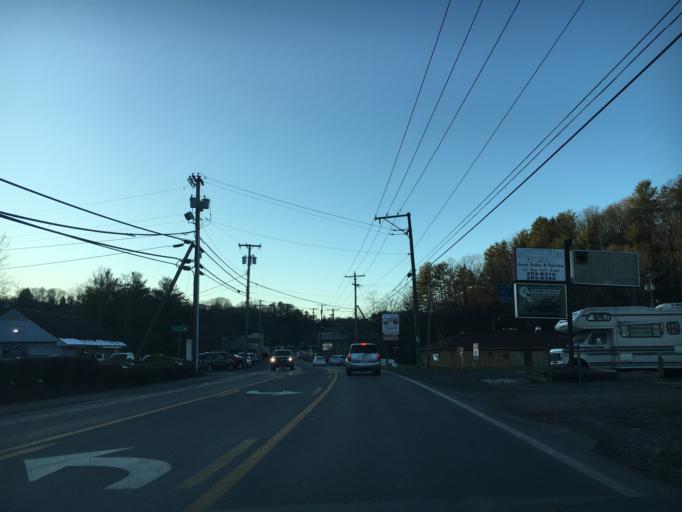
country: US
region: West Virginia
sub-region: Raleigh County
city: Beaver
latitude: 37.7496
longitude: -81.1384
